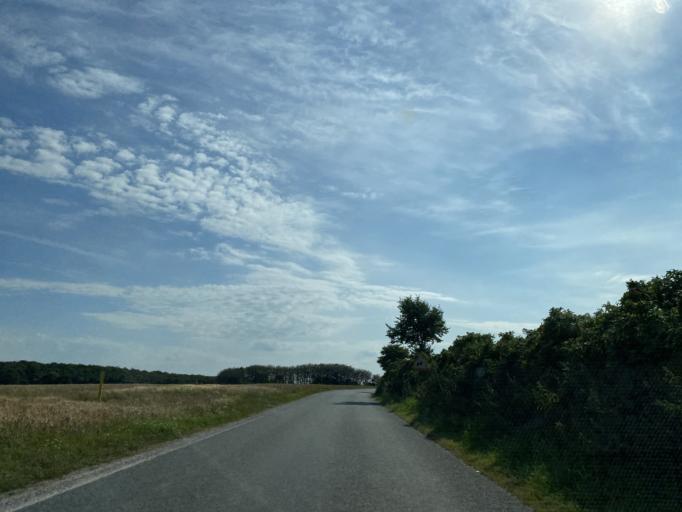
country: DK
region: Central Jutland
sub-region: Favrskov Kommune
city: Ulstrup
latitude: 56.3333
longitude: 9.7400
